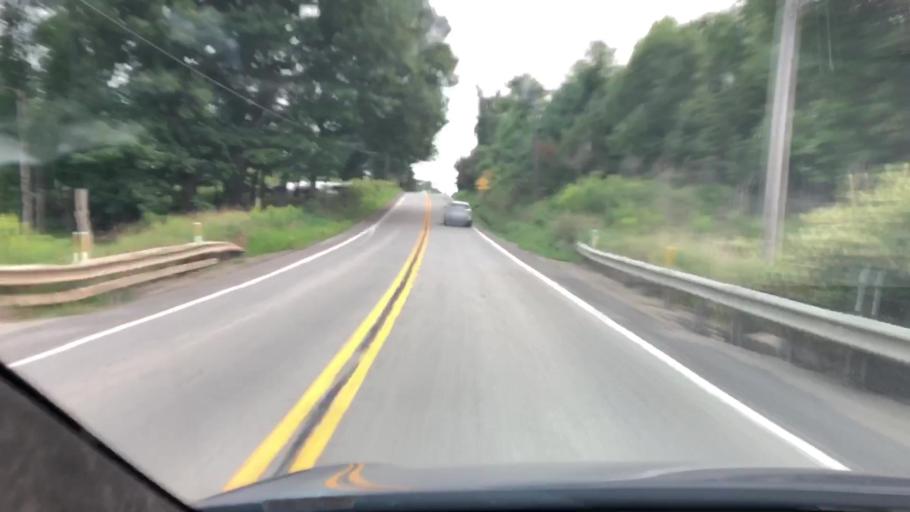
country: US
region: Pennsylvania
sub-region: Mercer County
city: Grove City
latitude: 41.1564
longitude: -80.0028
